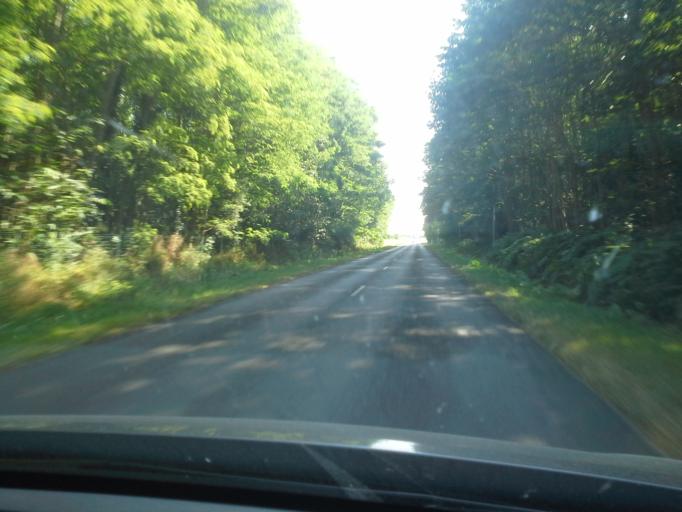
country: FR
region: Centre
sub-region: Departement du Loir-et-Cher
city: Cande-sur-Beuvron
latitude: 47.5006
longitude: 1.2706
